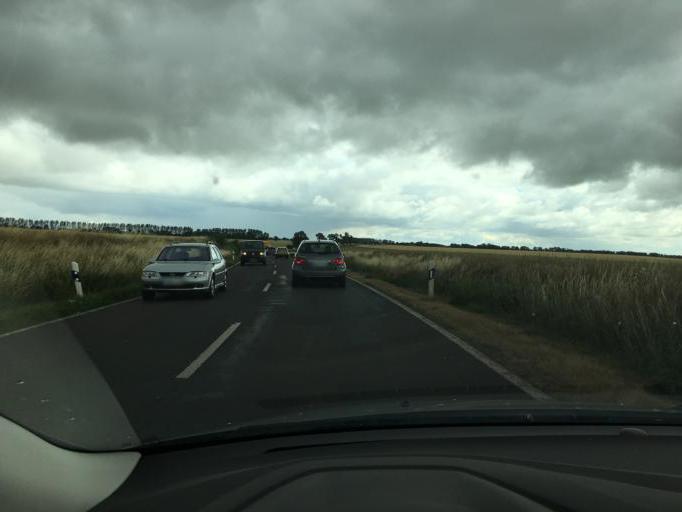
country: DE
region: Saxony-Anhalt
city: Wanzleben
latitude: 52.0660
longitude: 11.4529
